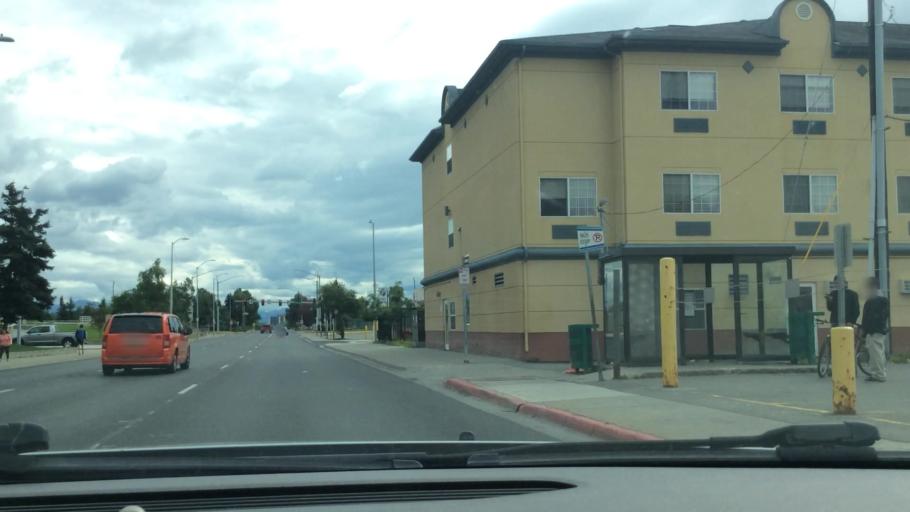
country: US
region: Alaska
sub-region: Anchorage Municipality
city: Anchorage
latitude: 61.2153
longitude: -149.8873
